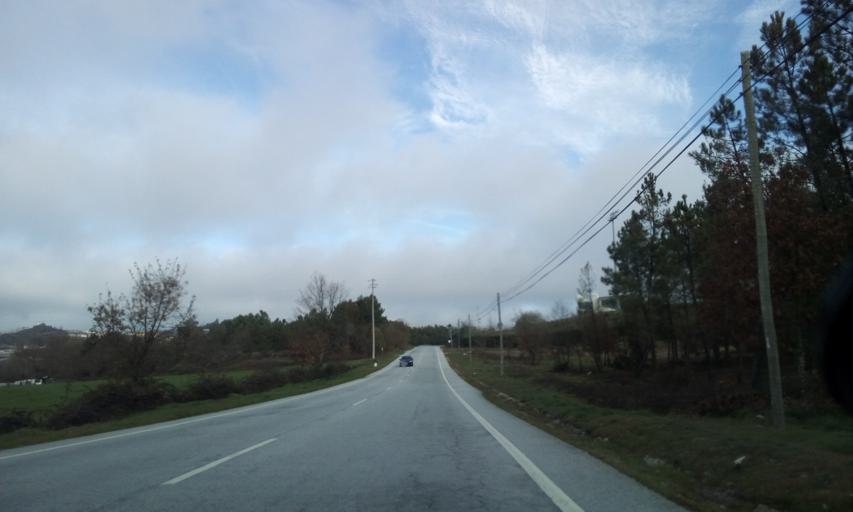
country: PT
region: Guarda
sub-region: Aguiar da Beira
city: Aguiar da Beira
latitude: 40.8105
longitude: -7.5336
